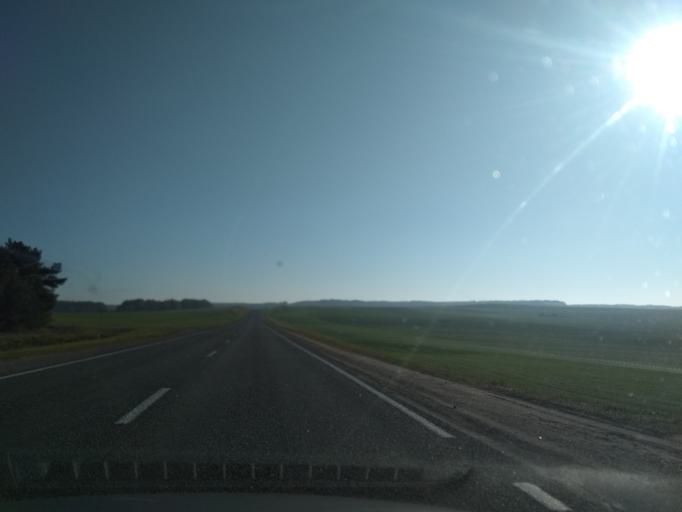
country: BY
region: Grodnenskaya
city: Zel'va
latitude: 53.1457
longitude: 24.8635
